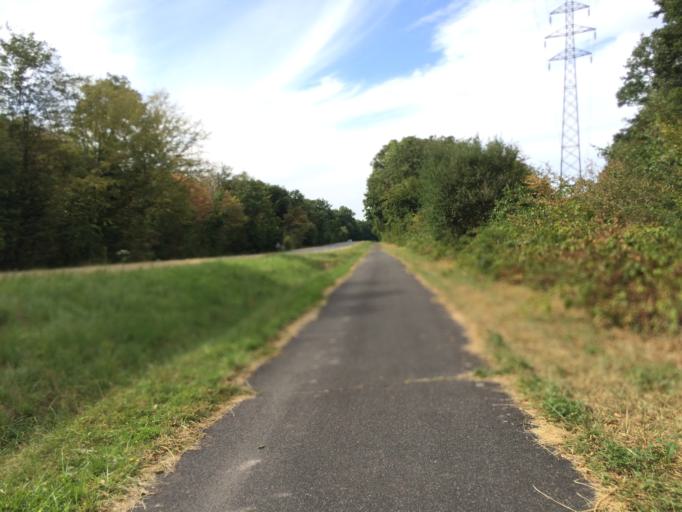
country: FR
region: Ile-de-France
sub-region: Departement de l'Essonne
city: Quincy-sous-Senart
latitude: 48.6688
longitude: 2.5276
